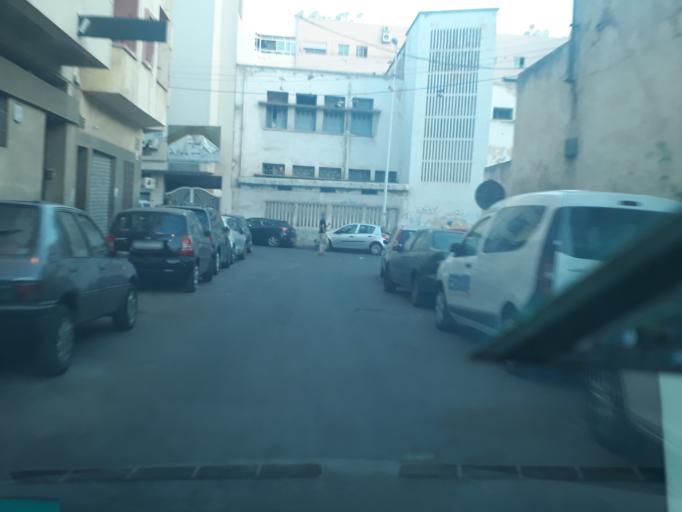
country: MA
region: Grand Casablanca
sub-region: Casablanca
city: Casablanca
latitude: 33.5766
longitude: -7.6432
